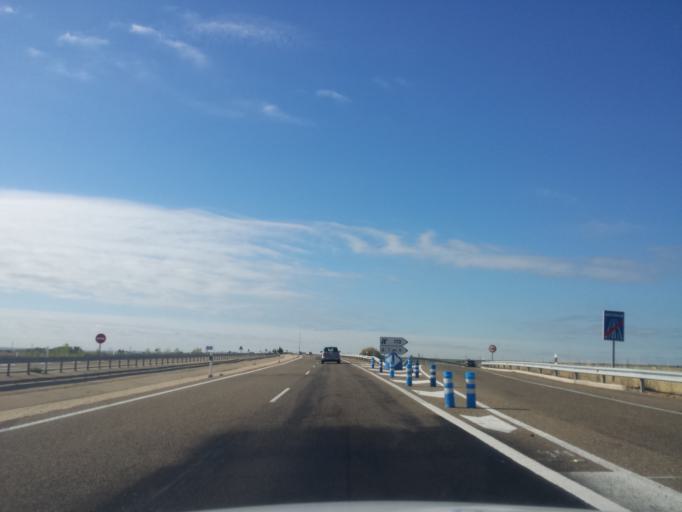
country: ES
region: Castille and Leon
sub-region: Provincia de Leon
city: Villamanan
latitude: 42.3297
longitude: -5.6097
